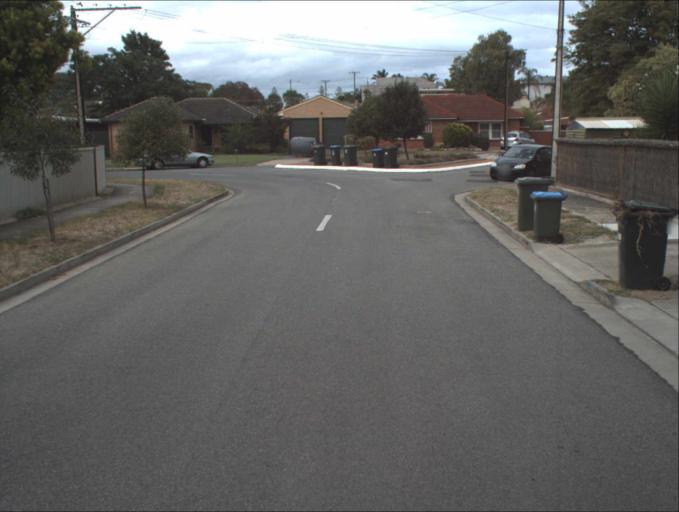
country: AU
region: South Australia
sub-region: Port Adelaide Enfield
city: Birkenhead
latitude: -34.8047
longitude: 138.4924
